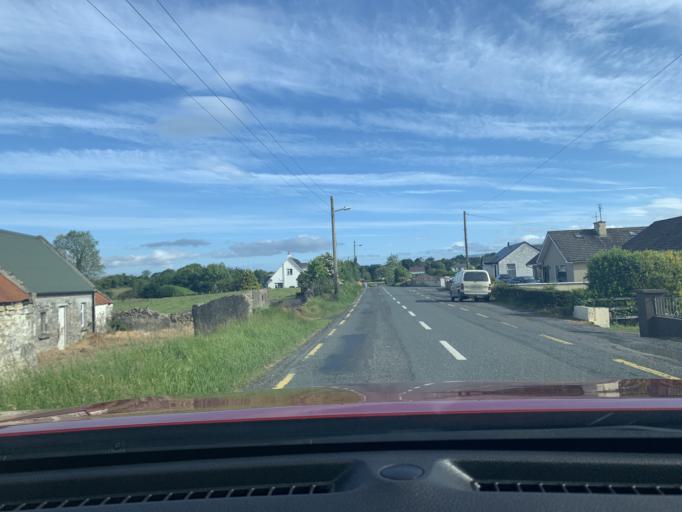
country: IE
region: Connaught
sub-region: Sligo
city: Sligo
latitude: 54.2376
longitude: -8.4728
